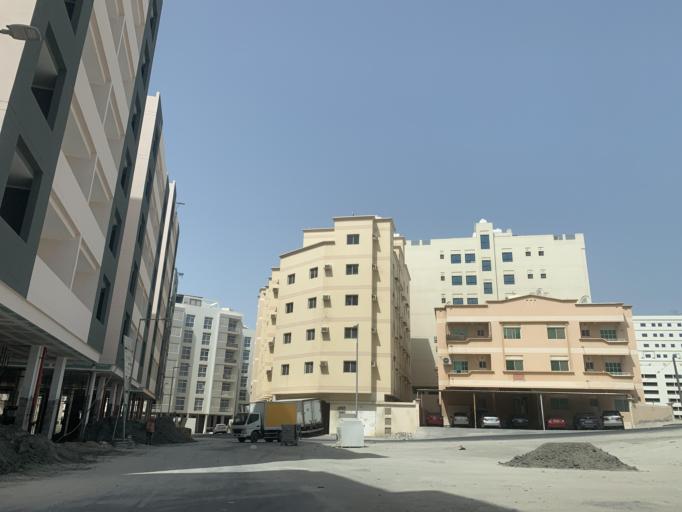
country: BH
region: Northern
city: Ar Rifa'
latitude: 26.1530
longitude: 50.5664
